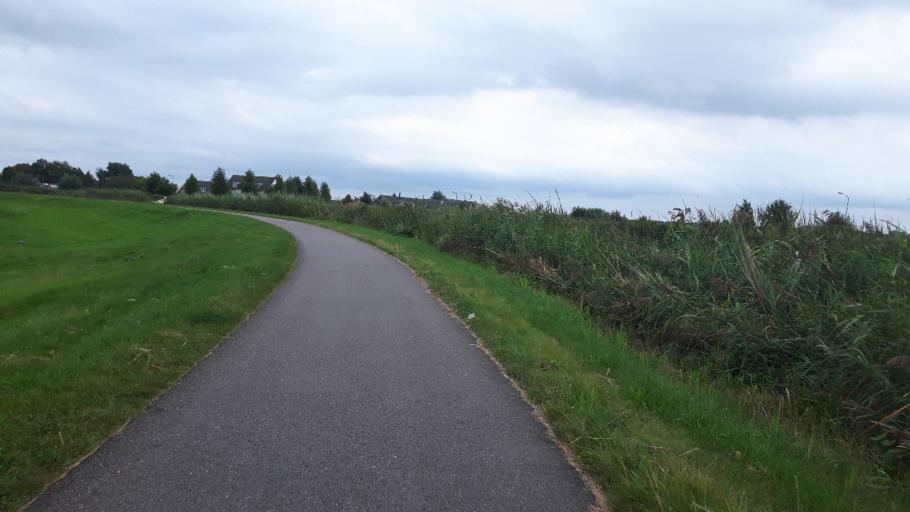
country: NL
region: North Holland
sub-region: Gemeente Ouder-Amstel
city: Ouderkerk aan de Amstel
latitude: 52.2800
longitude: 4.9270
